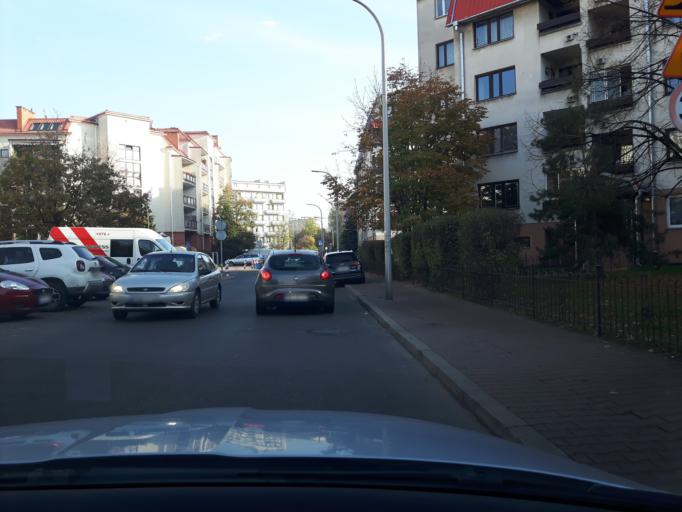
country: PL
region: Masovian Voivodeship
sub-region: Warszawa
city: Ochota
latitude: 52.2110
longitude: 20.9633
